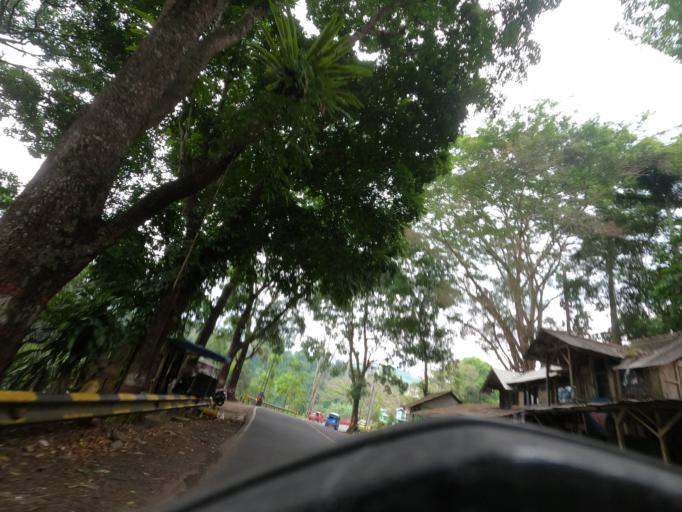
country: ID
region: West Java
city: Ciranjang-hilir
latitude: -6.7941
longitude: 107.0767
